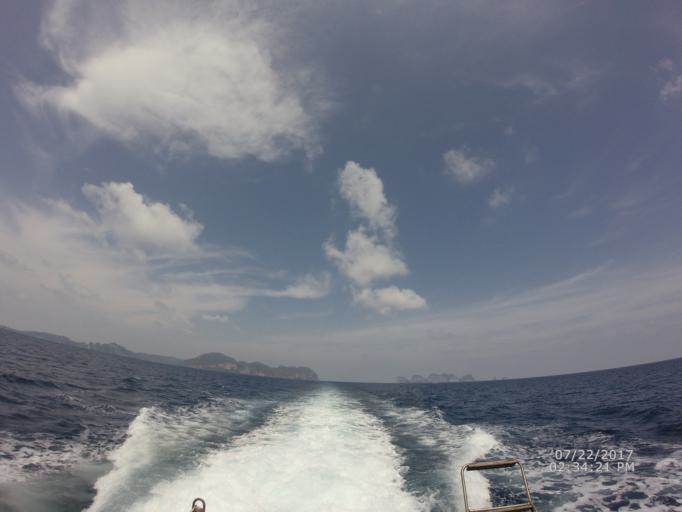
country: TH
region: Phangnga
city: Ban Phru Nai
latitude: 7.7428
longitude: 98.7068
